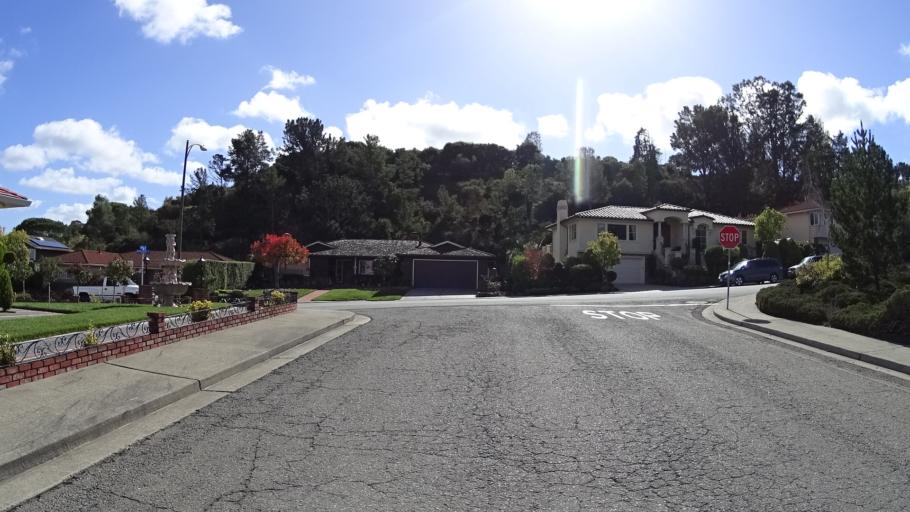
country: US
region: California
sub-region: San Mateo County
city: Millbrae
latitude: 37.5917
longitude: -122.3978
